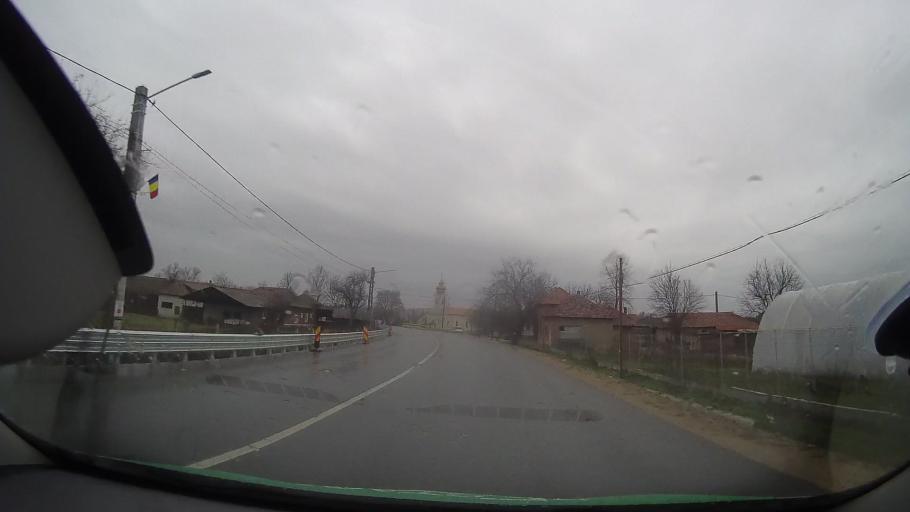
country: RO
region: Bihor
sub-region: Comuna Pocola
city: Pocola
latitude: 46.6936
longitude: 22.2951
